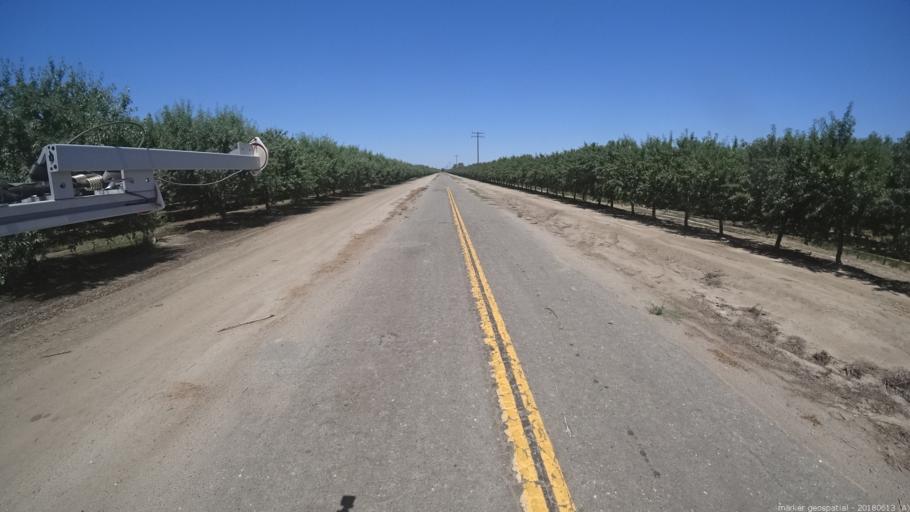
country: US
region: California
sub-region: Madera County
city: Chowchilla
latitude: 37.0548
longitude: -120.2745
